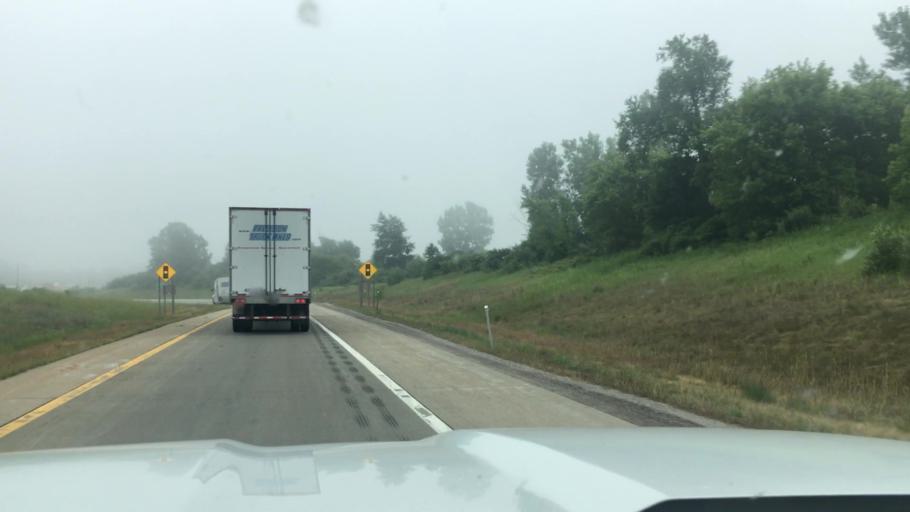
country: US
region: Michigan
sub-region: Shiawassee County
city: Perry
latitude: 42.8382
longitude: -84.2232
